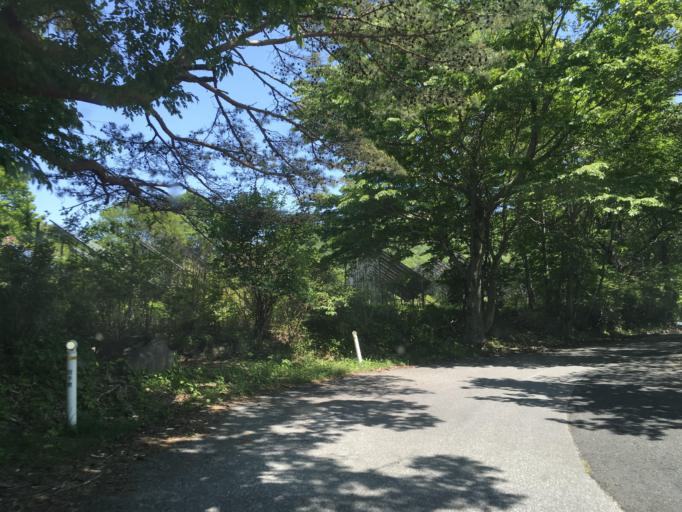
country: JP
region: Iwate
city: Ofunato
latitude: 39.1742
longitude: 141.7299
